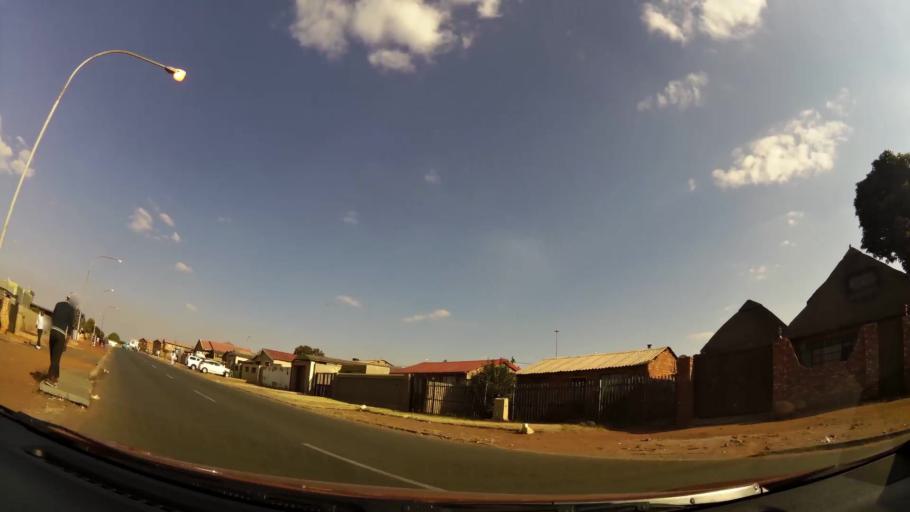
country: ZA
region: Gauteng
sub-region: City of Johannesburg Metropolitan Municipality
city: Soweto
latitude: -26.2279
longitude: 27.8740
